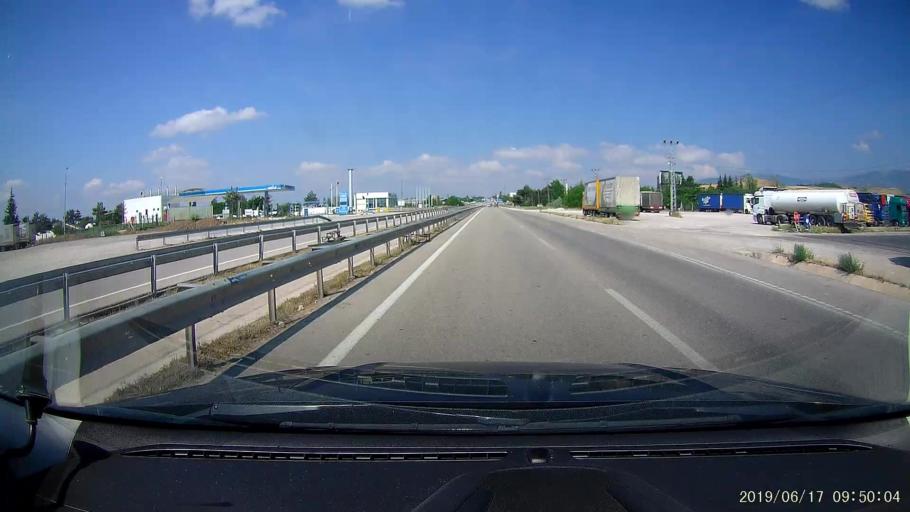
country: TR
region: Amasya
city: Merzifon
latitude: 40.8717
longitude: 35.5159
